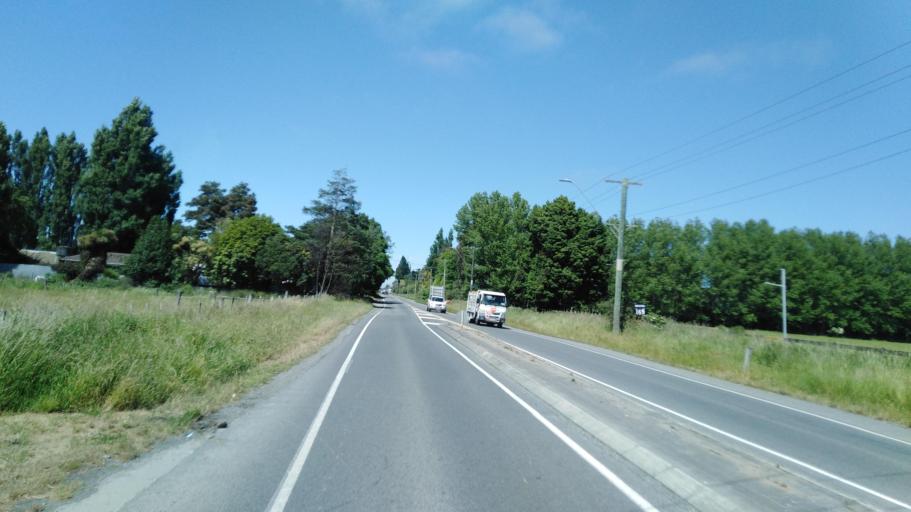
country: NZ
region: Canterbury
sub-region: Selwyn District
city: Prebbleton
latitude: -43.5199
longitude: 172.5047
